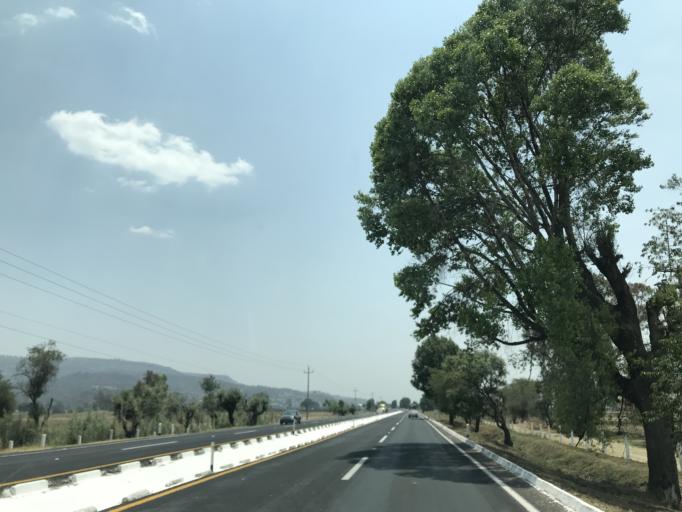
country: MX
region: Tlaxcala
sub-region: Ixtacuixtla de Mariano Matamoros
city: Santa Justina Ecatepec
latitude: 19.3265
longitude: -98.3250
